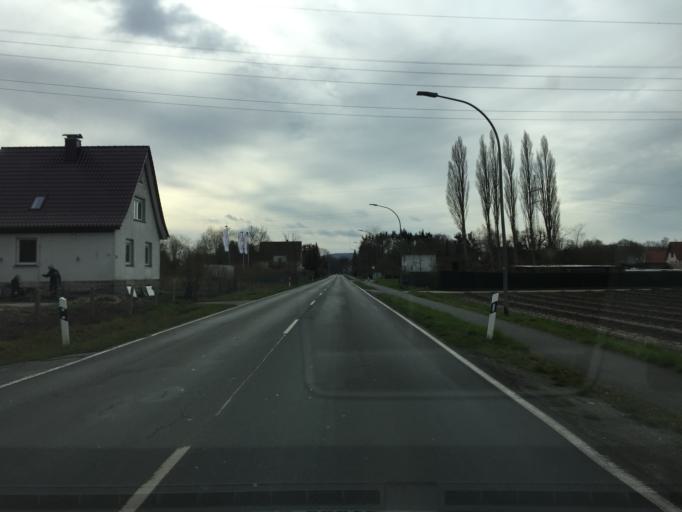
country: DE
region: North Rhine-Westphalia
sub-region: Regierungsbezirk Detmold
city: Lage
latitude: 51.9779
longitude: 8.7984
